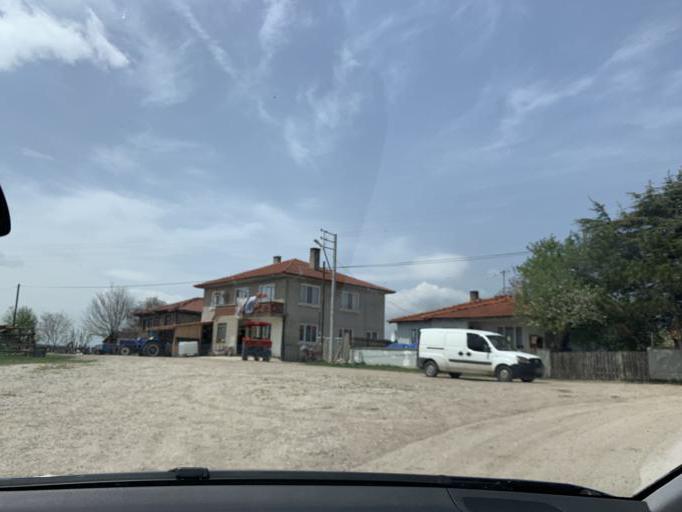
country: TR
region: Bolu
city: Bolu
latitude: 40.7665
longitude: 31.7059
